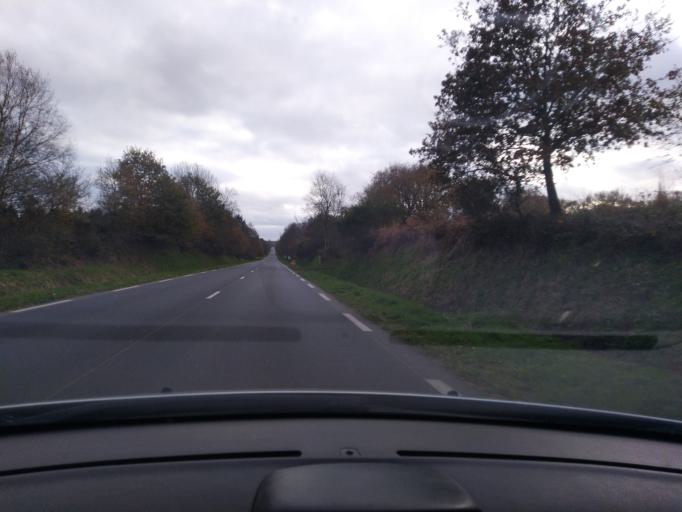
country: FR
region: Brittany
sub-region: Departement des Cotes-d'Armor
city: Plouaret
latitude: 48.5803
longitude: -3.4946
